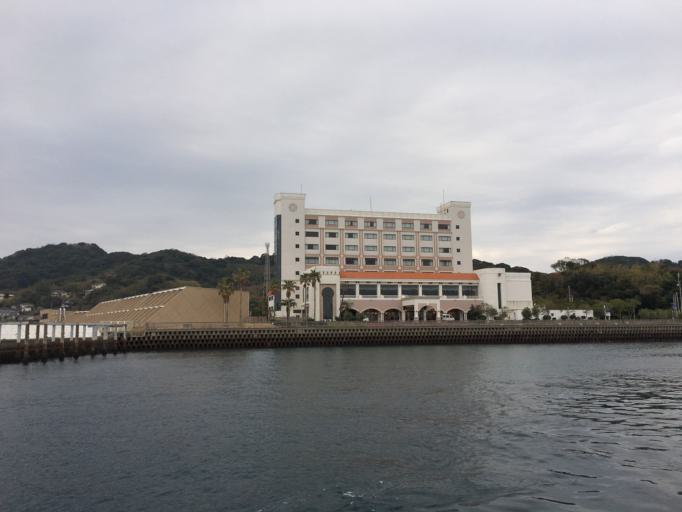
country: JP
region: Nagasaki
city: Nagasaki-shi
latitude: 32.7031
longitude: 129.7807
